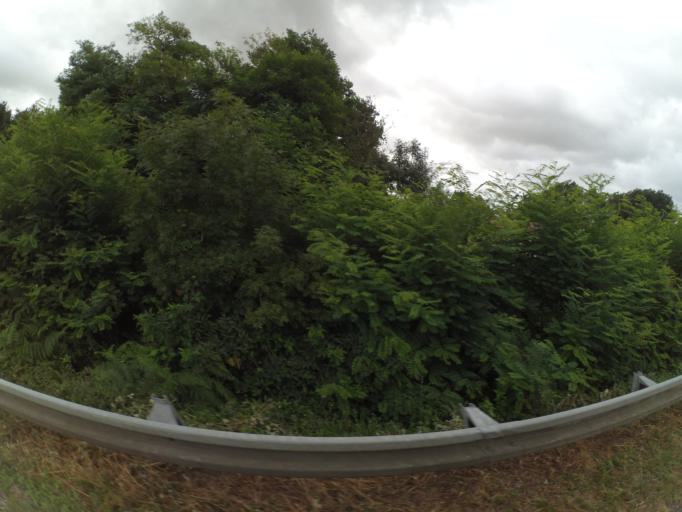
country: FR
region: Pays de la Loire
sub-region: Departement de Maine-et-Loire
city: Montfaucon-Montigne
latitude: 47.1115
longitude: -1.1085
